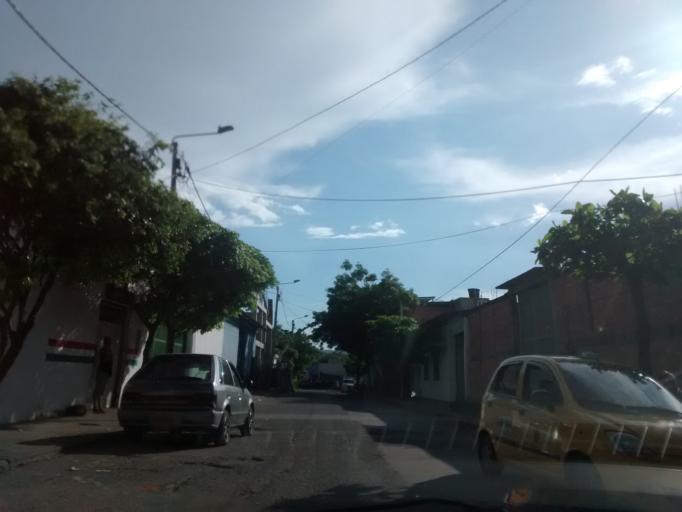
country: CO
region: Cundinamarca
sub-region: Girardot
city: Girardot City
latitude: 4.3081
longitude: -74.8028
